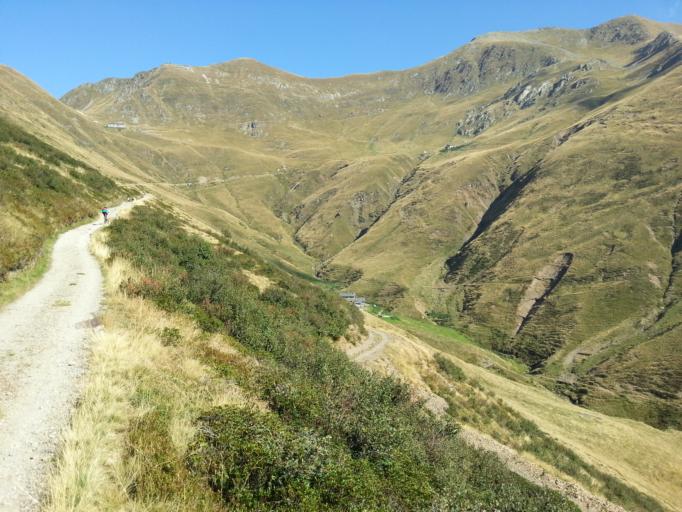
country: IT
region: Lombardy
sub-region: Provincia di Como
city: San Bartolomeo Val Cavargna
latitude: 46.1588
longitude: 9.1660
